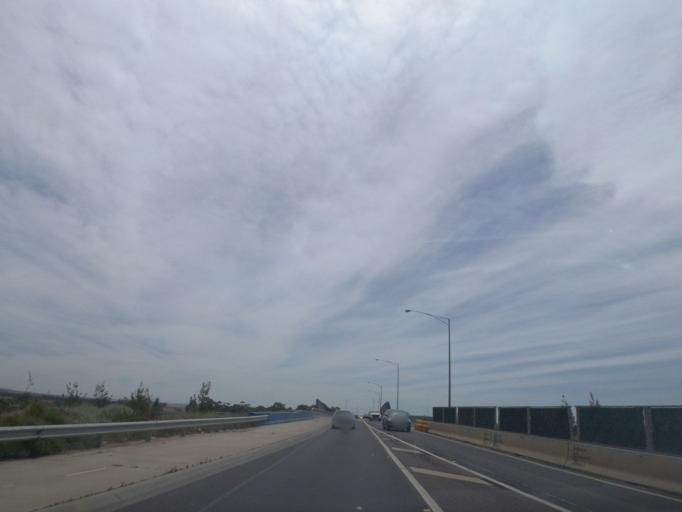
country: AU
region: Victoria
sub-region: Wyndham
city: Tarneit
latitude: -37.8328
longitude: 144.6913
